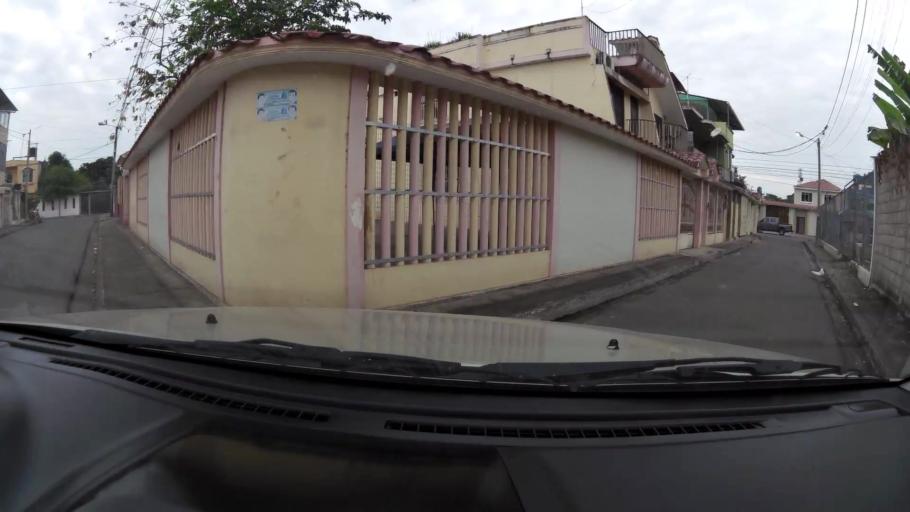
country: EC
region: El Oro
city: Machala
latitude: -3.2649
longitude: -79.9457
